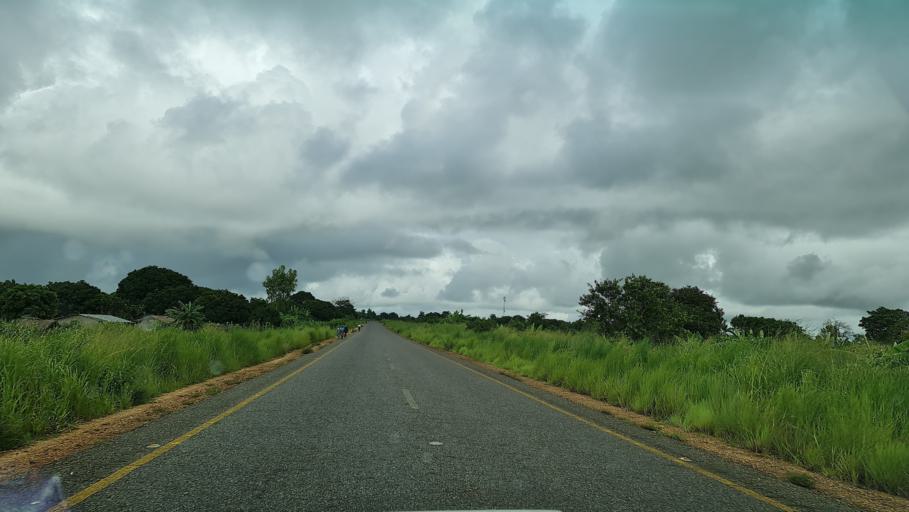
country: MZ
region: Nampula
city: Nampula
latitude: -15.0570
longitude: 38.4127
